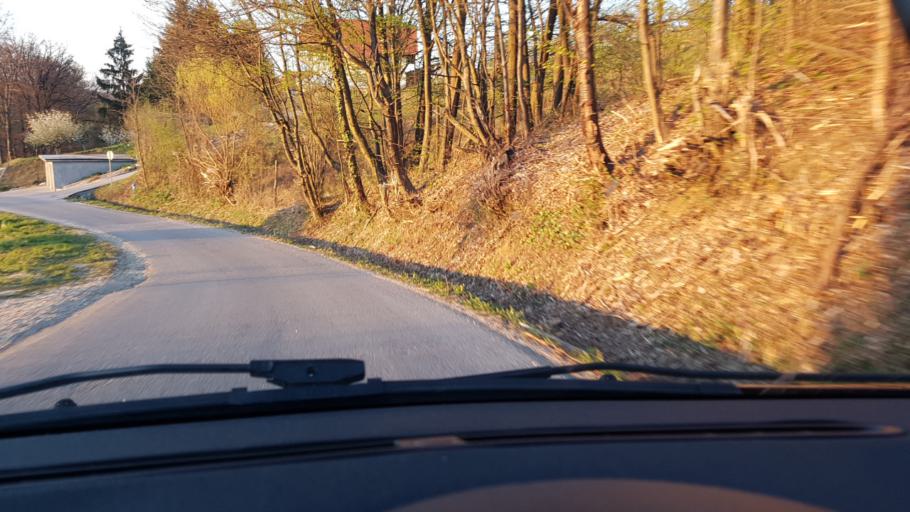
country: SI
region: Rogatec
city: Rogatec
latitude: 46.1869
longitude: 15.6842
